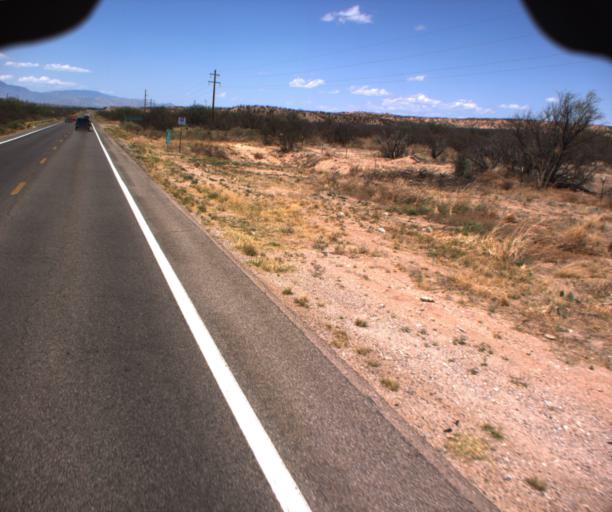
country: US
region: Arizona
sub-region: Cochise County
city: Saint David
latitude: 31.8455
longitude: -110.1941
